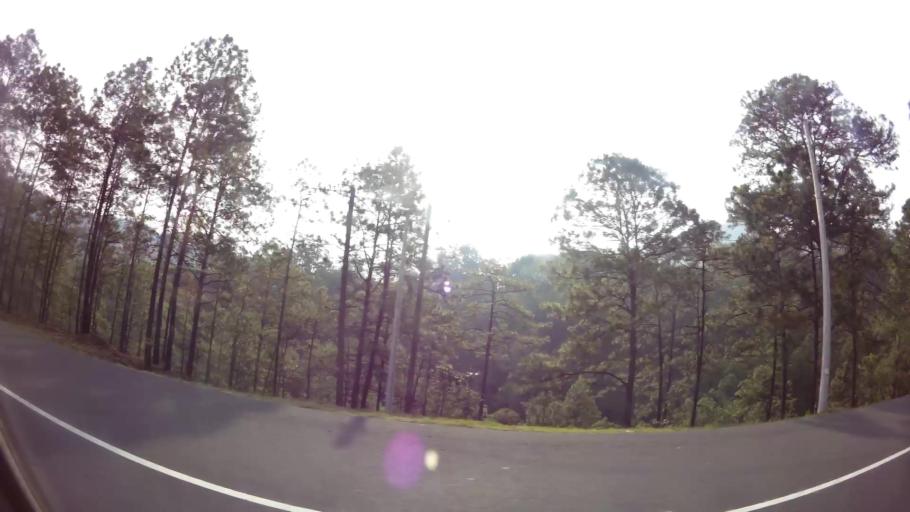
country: HN
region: Francisco Morazan
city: Zambrano
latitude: 14.2843
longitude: -87.4675
